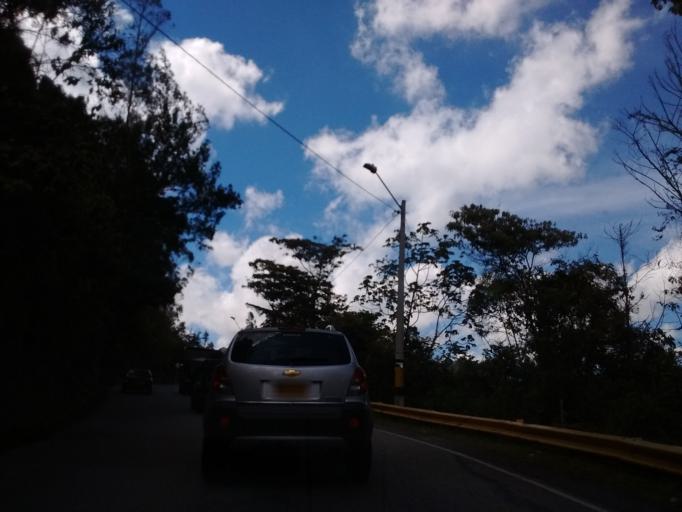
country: CO
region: Antioquia
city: Medellin
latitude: 6.2342
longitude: -75.5095
